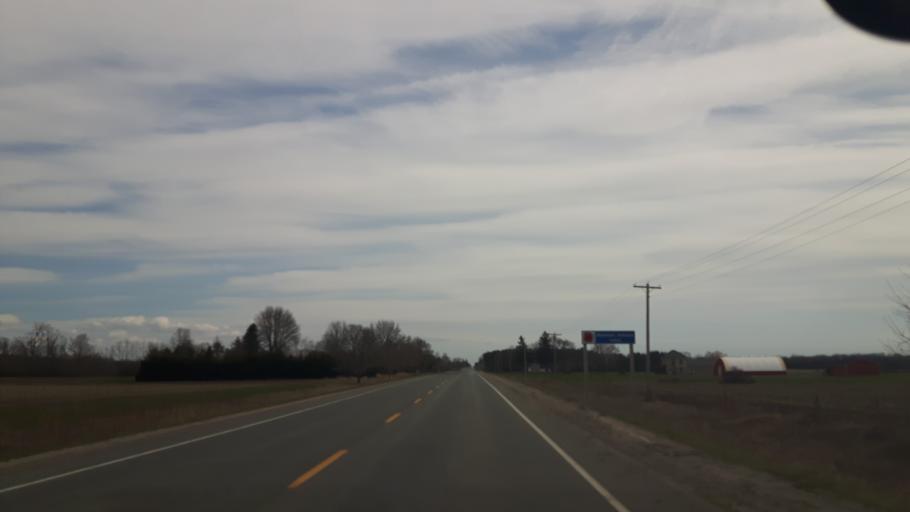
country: CA
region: Ontario
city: Goderich
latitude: 43.7147
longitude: -81.7058
